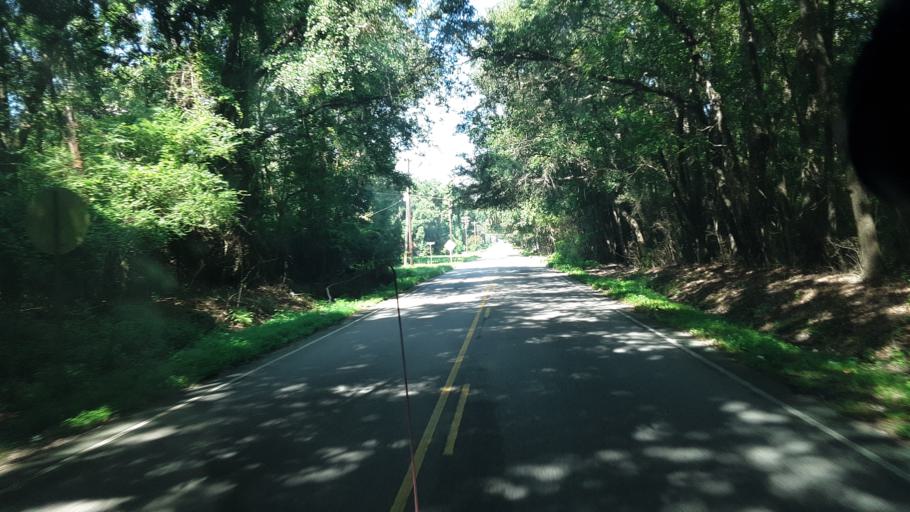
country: US
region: South Carolina
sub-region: Jasper County
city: Ridgeland
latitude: 32.5888
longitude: -80.9310
